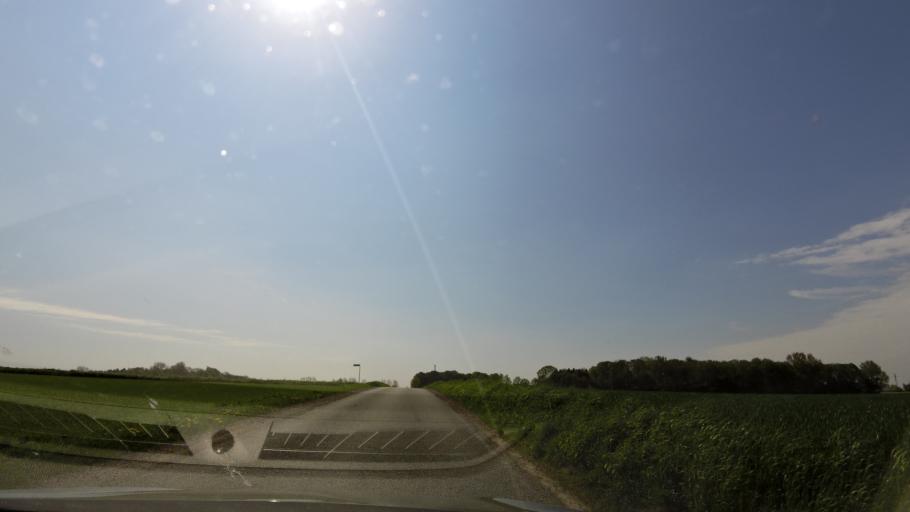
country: DK
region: South Denmark
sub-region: Nyborg Kommune
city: Ullerslev
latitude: 55.2725
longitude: 10.6893
